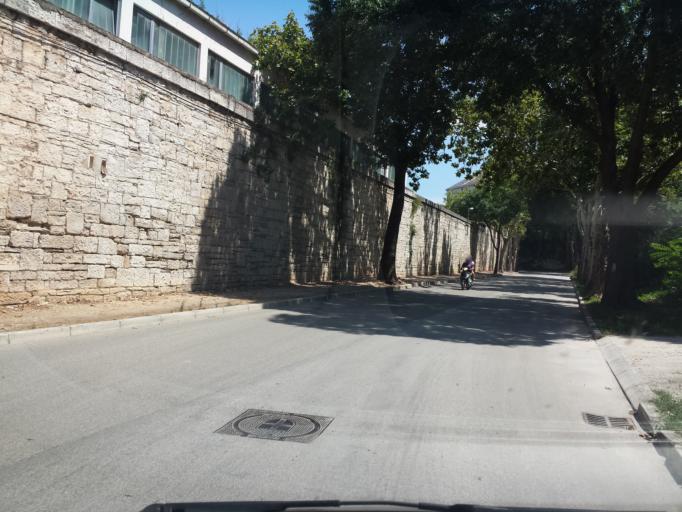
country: HR
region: Istarska
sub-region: Grad Pula
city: Pula
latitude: 44.8630
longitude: 13.8357
